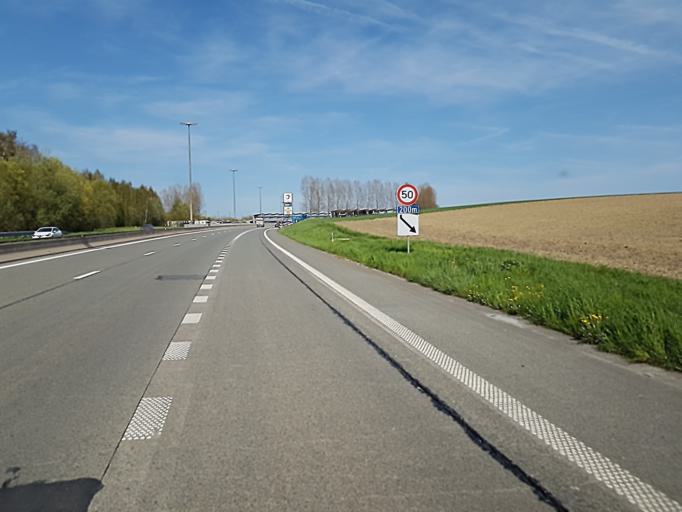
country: BE
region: Wallonia
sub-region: Province du Hainaut
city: Silly
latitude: 50.6809
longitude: 3.8923
